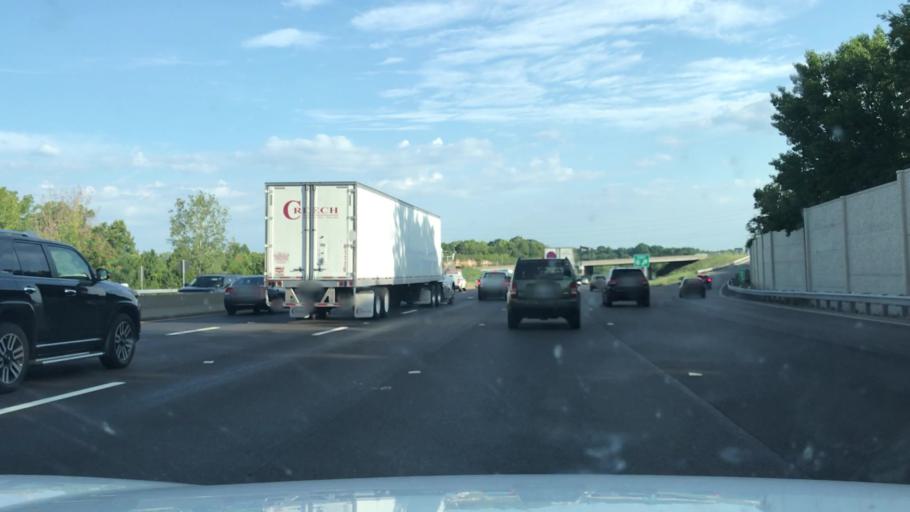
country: US
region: Missouri
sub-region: Saint Louis County
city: Des Peres
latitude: 38.5776
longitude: -90.4453
